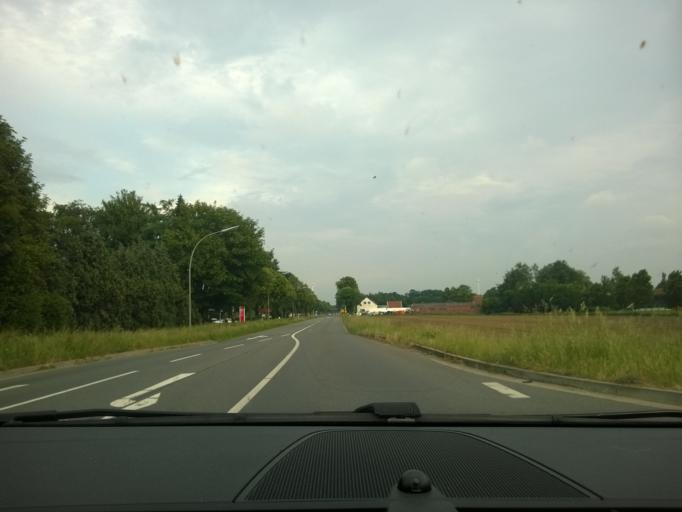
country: DE
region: North Rhine-Westphalia
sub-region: Regierungsbezirk Munster
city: Gescher
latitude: 51.9446
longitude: 7.0217
